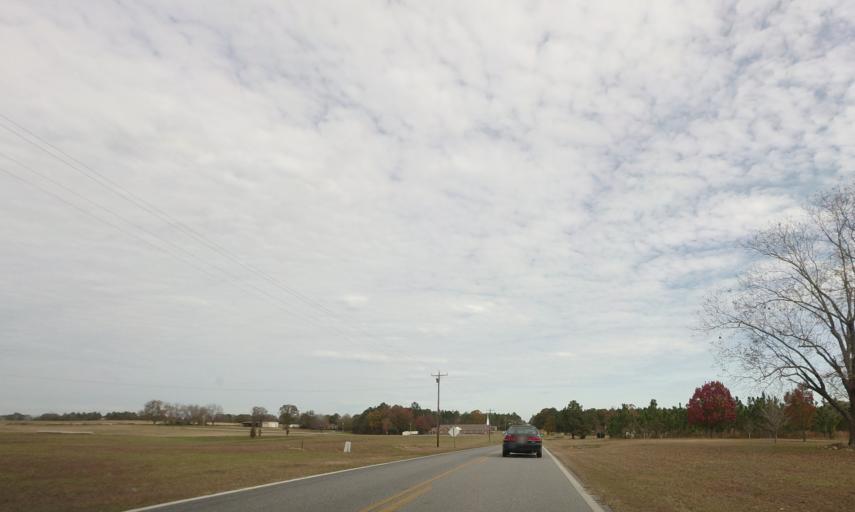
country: US
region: Georgia
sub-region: Dodge County
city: Chester
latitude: 32.4294
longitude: -83.1790
